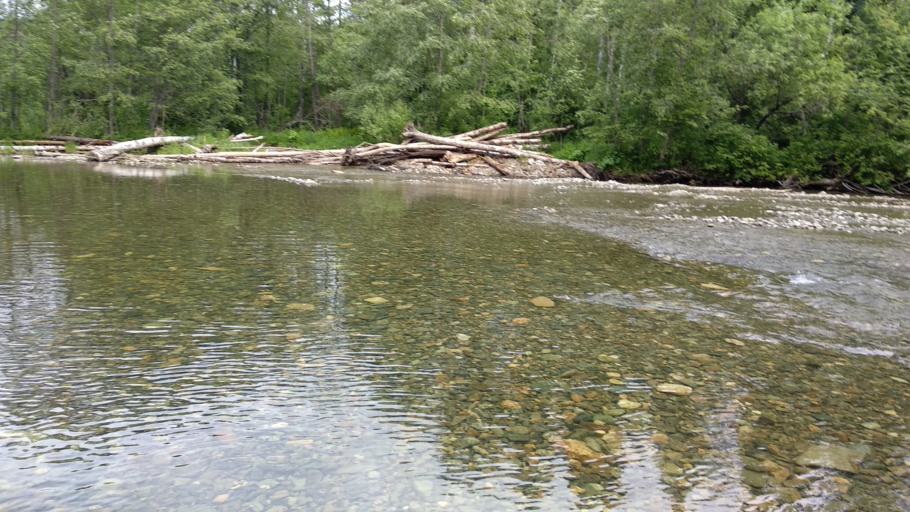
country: RU
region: Sverdlovsk
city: Karpinsk
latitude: 59.8012
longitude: 59.3834
